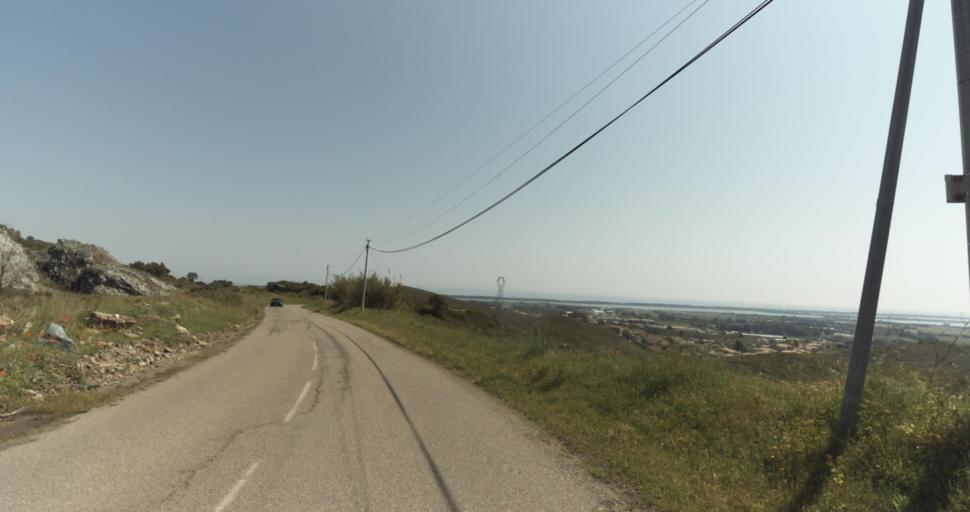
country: FR
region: Corsica
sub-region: Departement de la Haute-Corse
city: Biguglia
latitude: 42.6142
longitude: 9.4205
